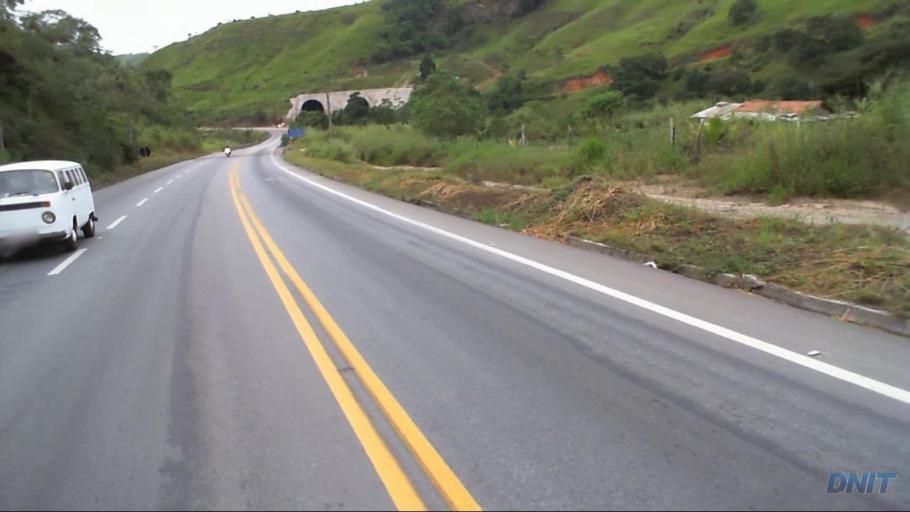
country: BR
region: Minas Gerais
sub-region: Timoteo
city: Timoteo
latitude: -19.6181
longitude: -42.7977
